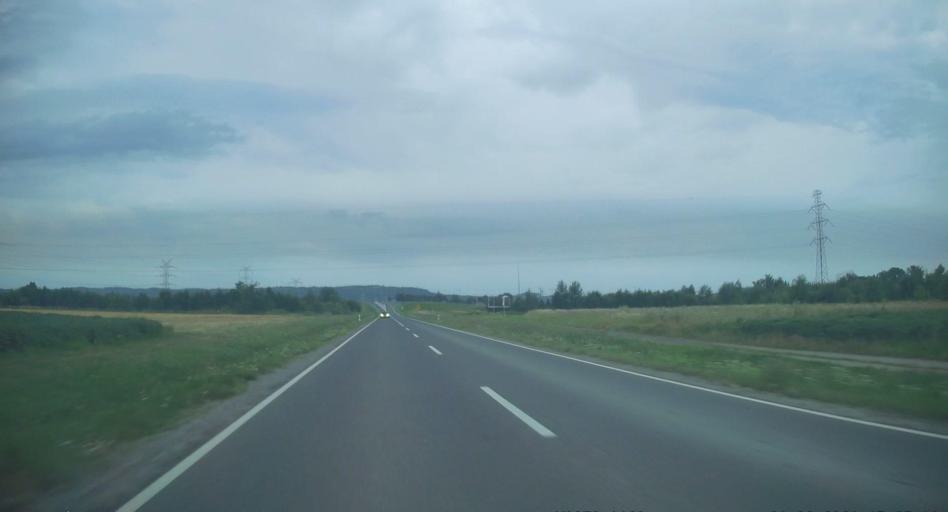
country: PL
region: Lesser Poland Voivodeship
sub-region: Powiat tarnowski
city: Wojnicz
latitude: 49.9678
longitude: 20.8470
